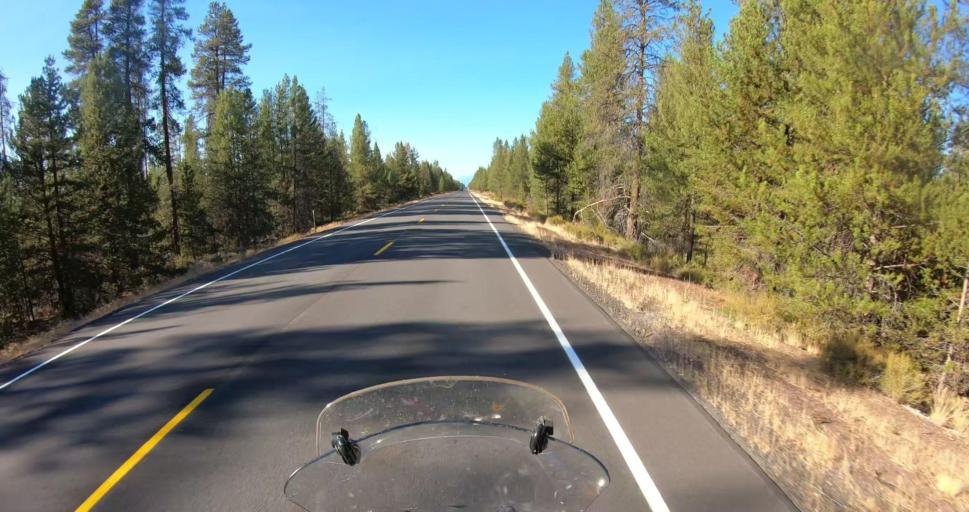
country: US
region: Oregon
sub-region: Deschutes County
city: La Pine
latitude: 43.5248
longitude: -121.4578
